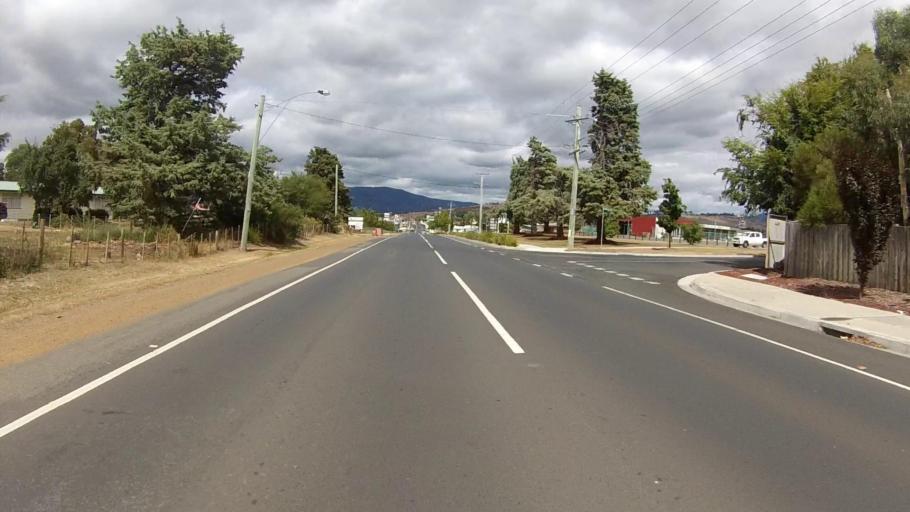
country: AU
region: Tasmania
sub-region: Brighton
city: Bridgewater
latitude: -42.6949
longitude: 147.2558
